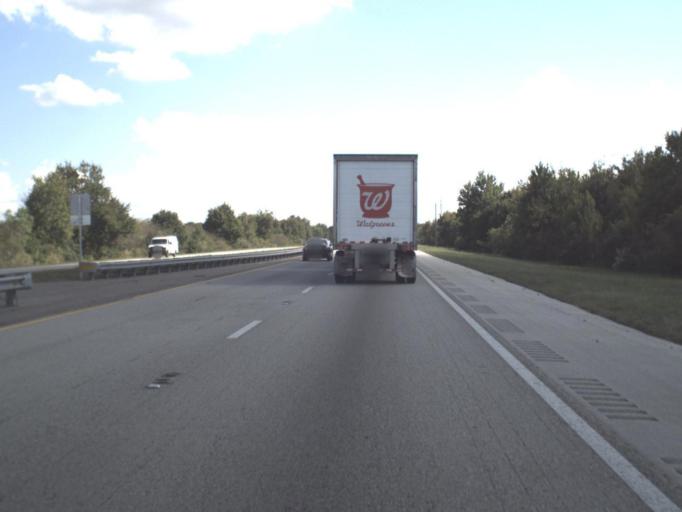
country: US
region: Florida
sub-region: Osceola County
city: Saint Cloud
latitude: 28.0372
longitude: -81.2021
